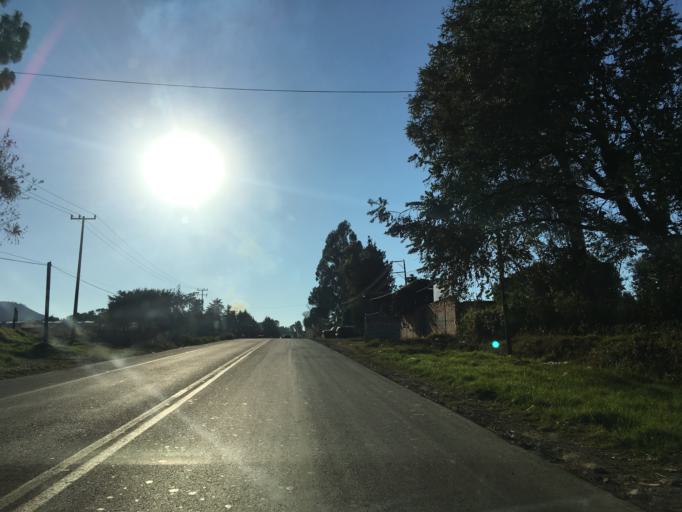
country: MX
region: Michoacan
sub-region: Zitacuaro
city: San Felipe los Alzati (Colonia Nueva)
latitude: 19.4886
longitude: -100.3796
